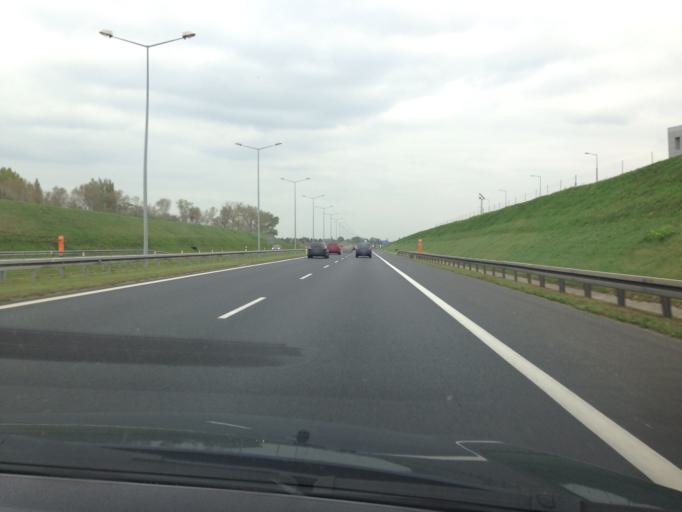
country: PL
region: Greater Poland Voivodeship
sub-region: Powiat poznanski
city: Lubon
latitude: 52.3526
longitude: 16.8650
